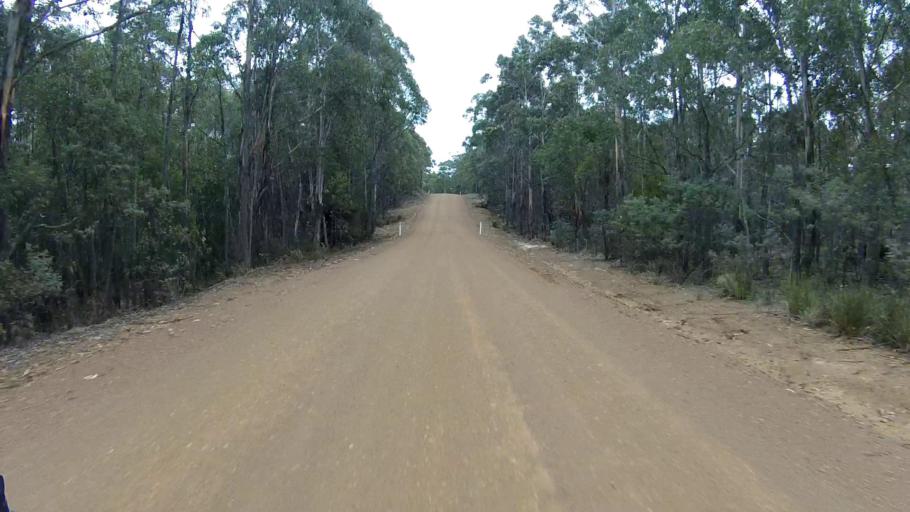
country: AU
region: Tasmania
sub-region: Sorell
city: Sorell
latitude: -42.5874
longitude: 147.8852
